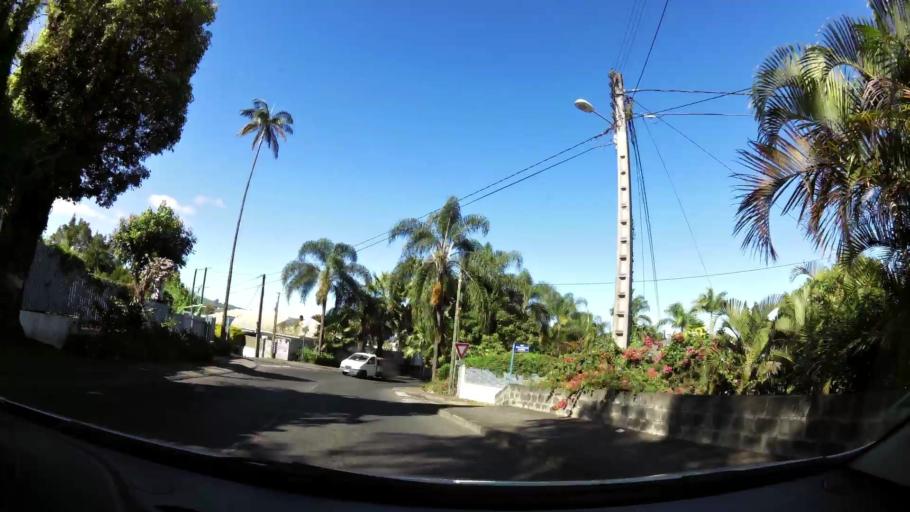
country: RE
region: Reunion
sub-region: Reunion
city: Le Tampon
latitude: -21.2769
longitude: 55.5247
